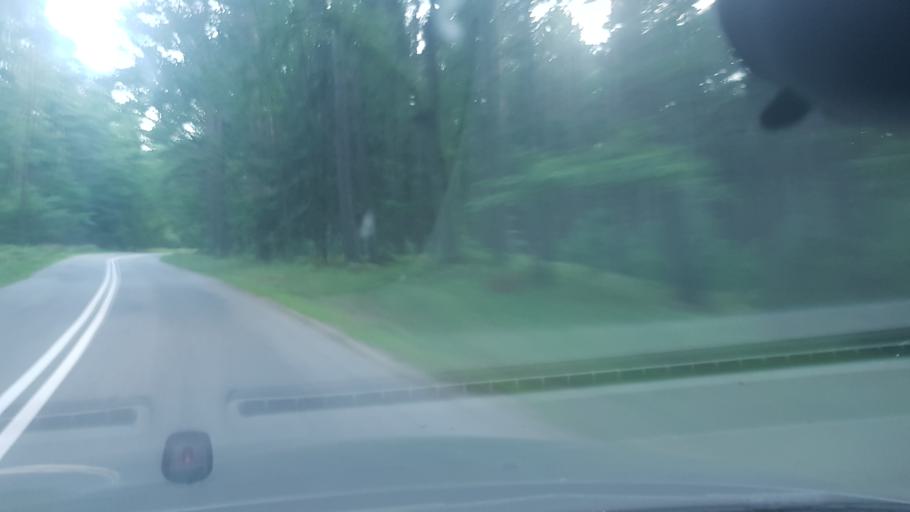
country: PL
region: Pomeranian Voivodeship
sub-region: Powiat nowodworski
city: Krynica Morska
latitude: 54.3566
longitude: 19.3211
